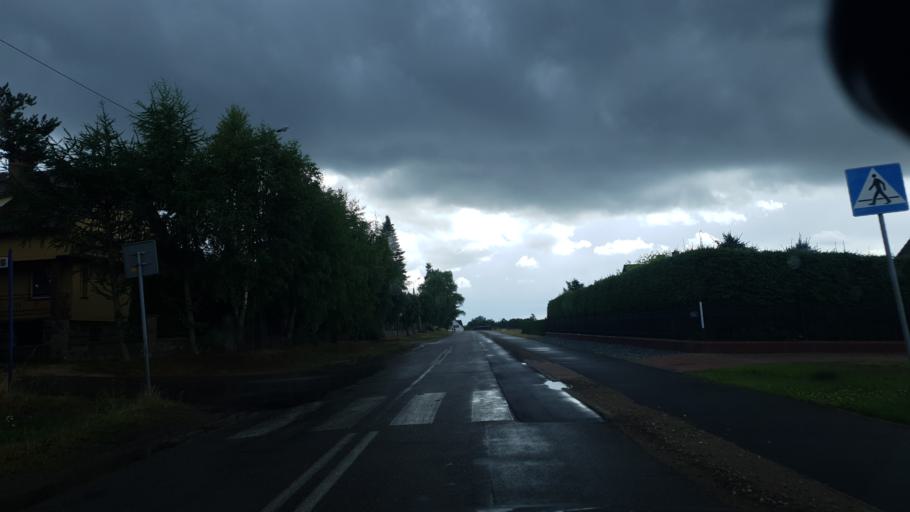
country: PL
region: Pomeranian Voivodeship
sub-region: Powiat kartuski
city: Stezyca
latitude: 54.2129
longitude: 17.9585
